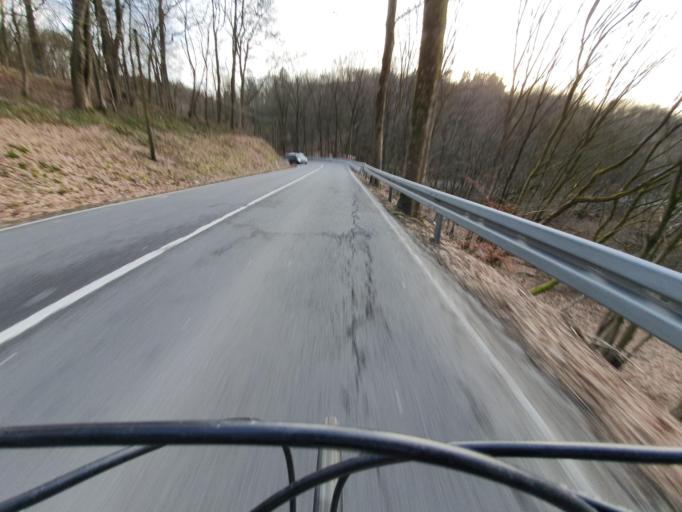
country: DE
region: North Rhine-Westphalia
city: Burscheid
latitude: 51.0892
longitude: 7.1748
